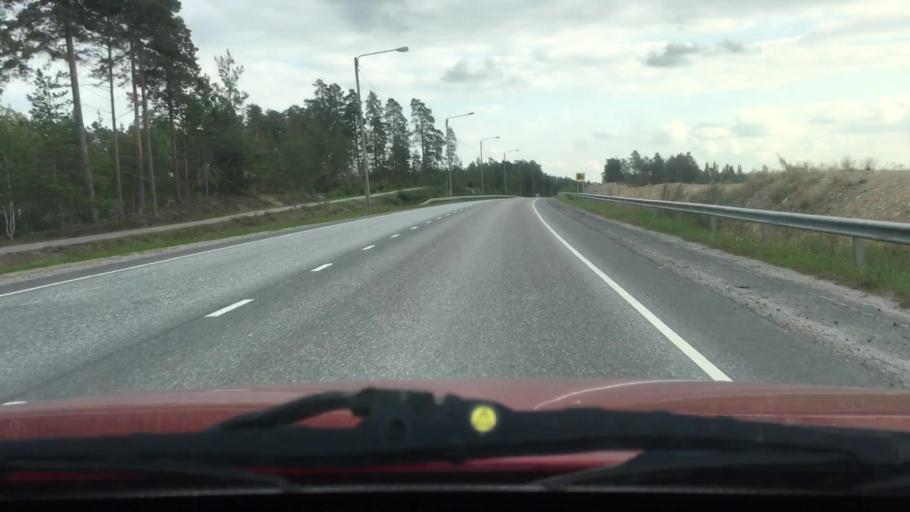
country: FI
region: Varsinais-Suomi
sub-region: Turku
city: Masku
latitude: 60.5473
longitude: 22.1264
